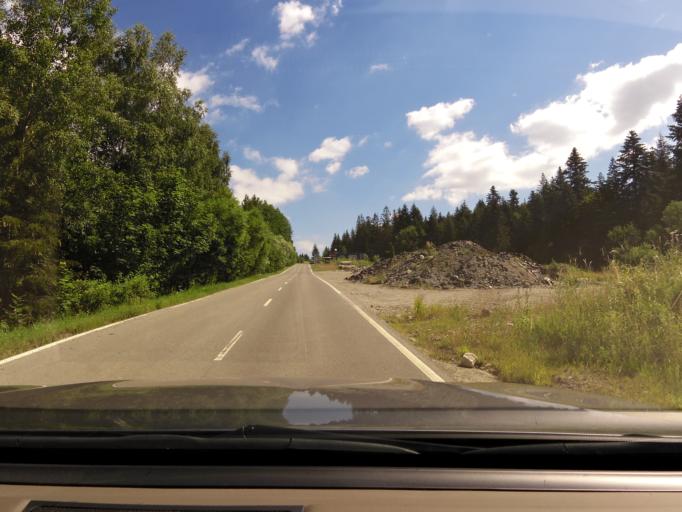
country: PL
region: Silesian Voivodeship
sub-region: Powiat cieszynski
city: Koniakow
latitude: 49.5057
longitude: 18.9555
